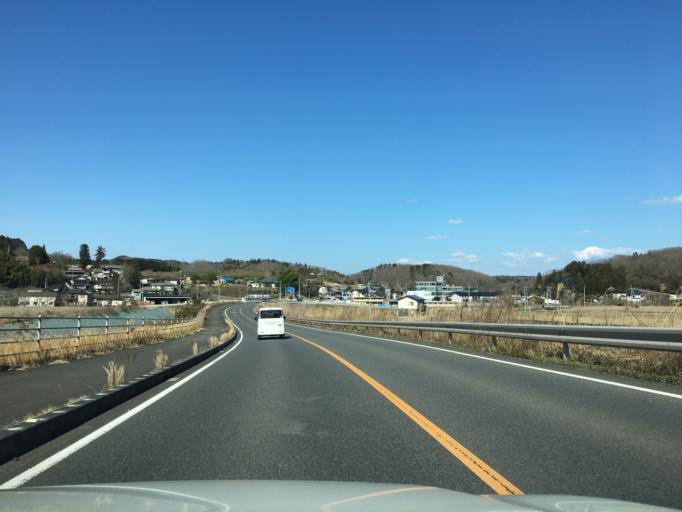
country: JP
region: Tochigi
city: Motegi
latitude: 36.5292
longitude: 140.1999
